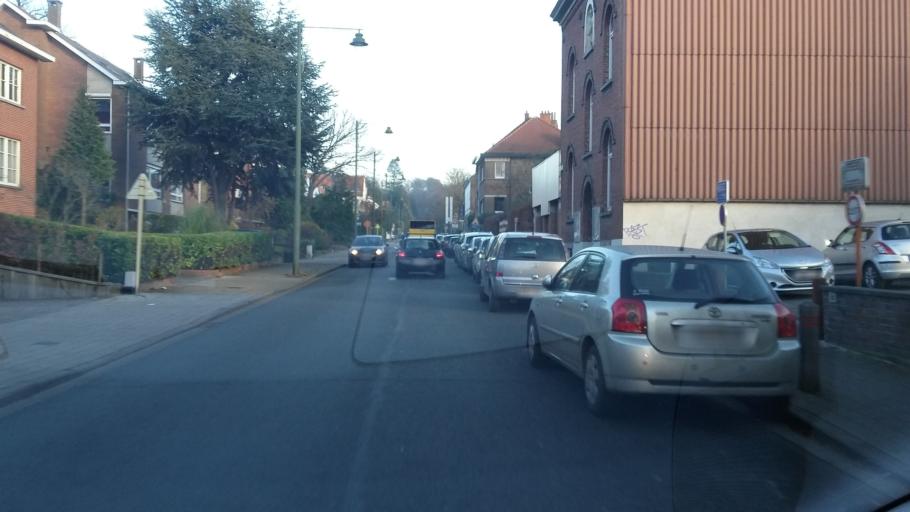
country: BE
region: Flanders
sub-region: Provincie Vlaams-Brabant
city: Kraainem
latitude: 50.8166
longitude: 4.4351
